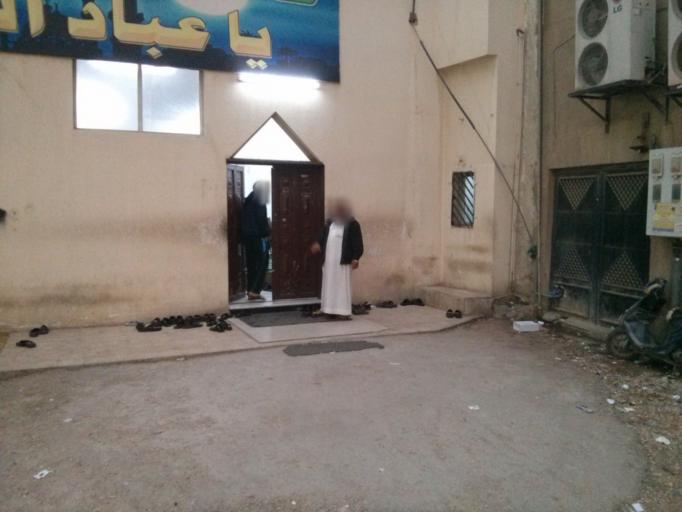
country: SA
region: Ar Riyad
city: Riyadh
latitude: 24.6382
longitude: 46.7221
